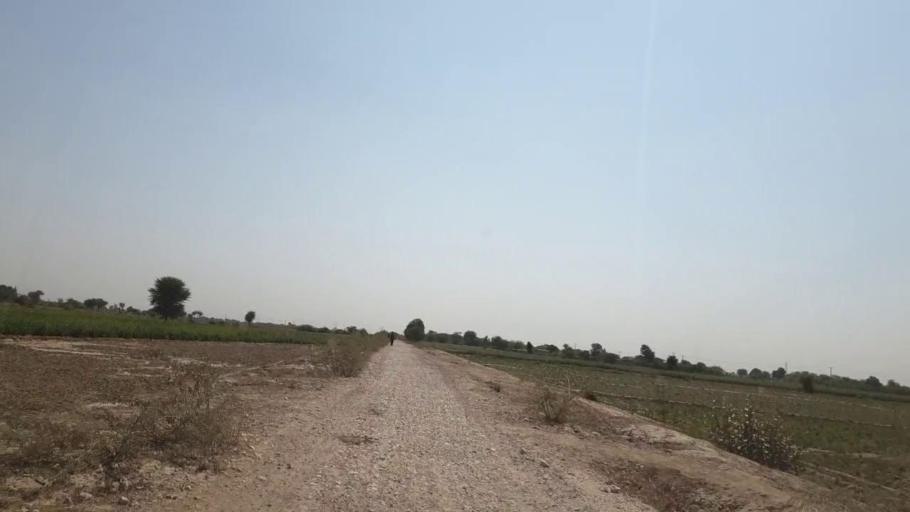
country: PK
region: Sindh
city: Kunri
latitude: 25.0887
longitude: 69.5317
